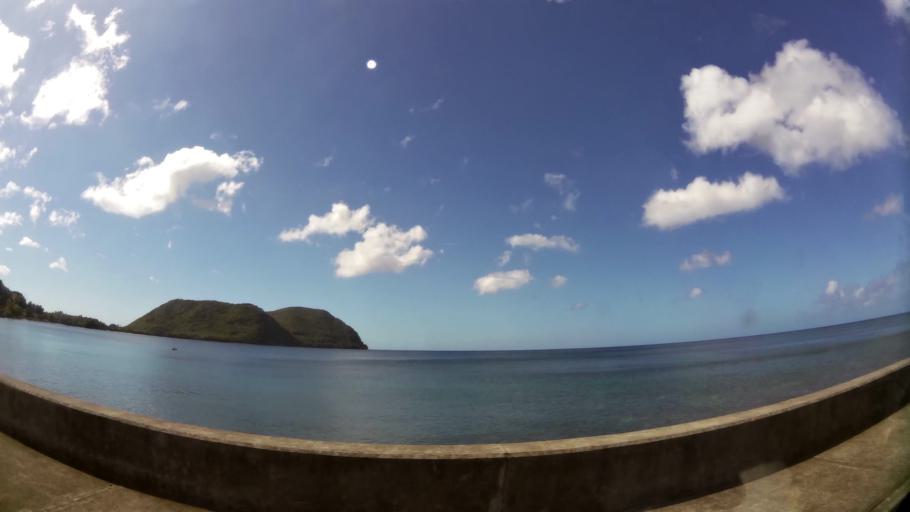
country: DM
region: Saint John
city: Portsmouth
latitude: 15.6003
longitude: -61.4620
